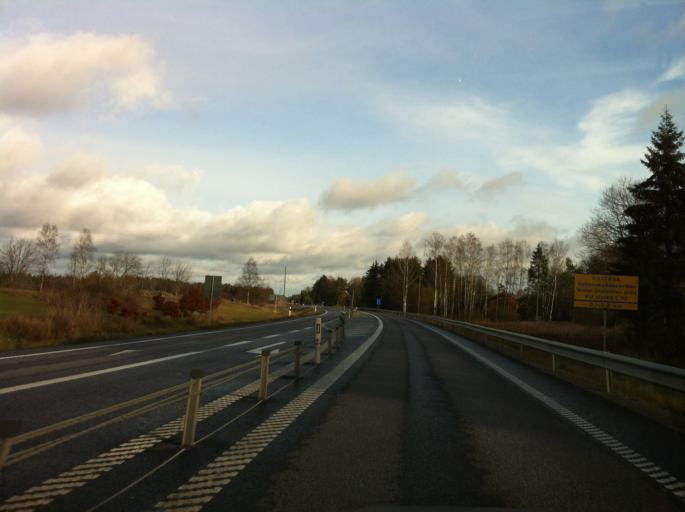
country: SE
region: Kronoberg
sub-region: Alvesta Kommun
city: Vislanda
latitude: 56.6999
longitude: 14.3544
